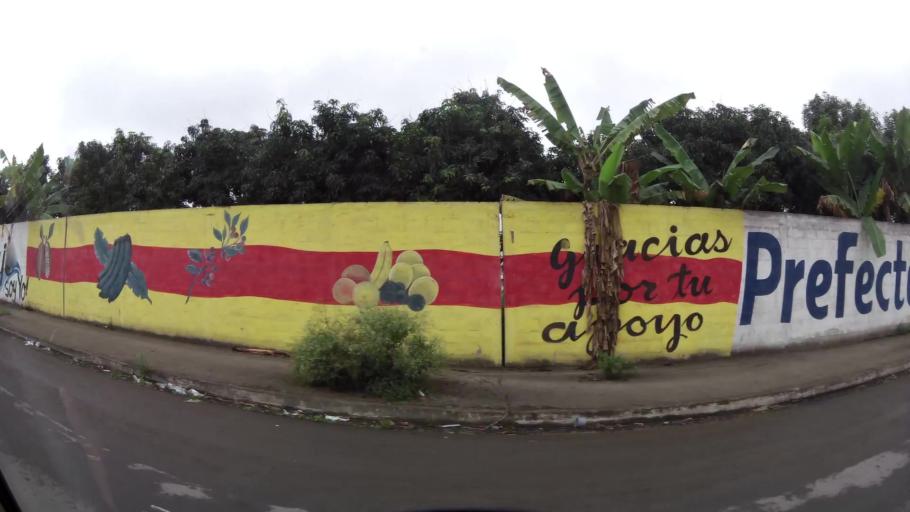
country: EC
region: El Oro
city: Pasaje
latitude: -3.3233
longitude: -79.8143
